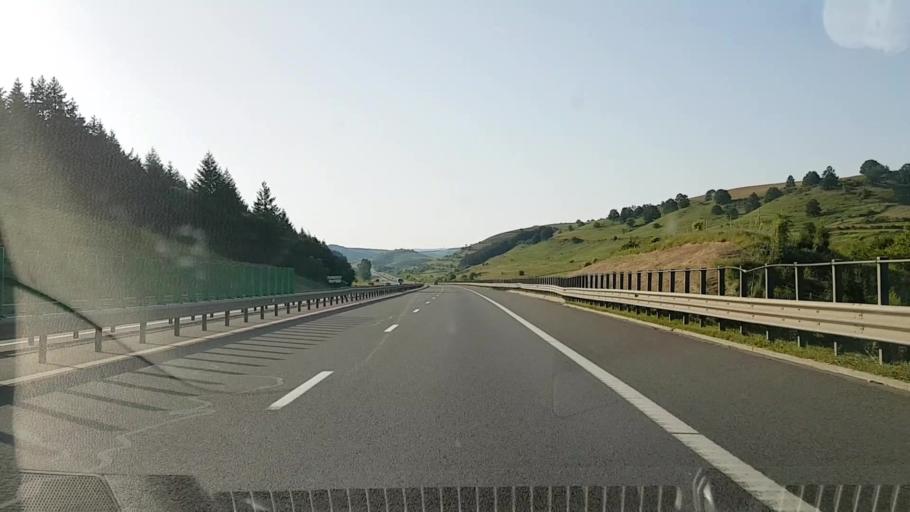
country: RO
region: Cluj
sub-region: Comuna Savadisla
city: Savadisla
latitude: 46.6704
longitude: 23.4847
